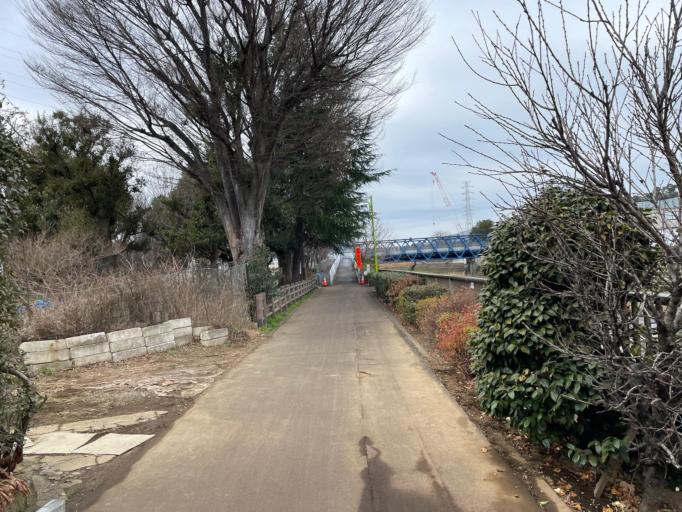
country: JP
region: Tokyo
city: Chofugaoka
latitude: 35.6292
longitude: 139.6035
